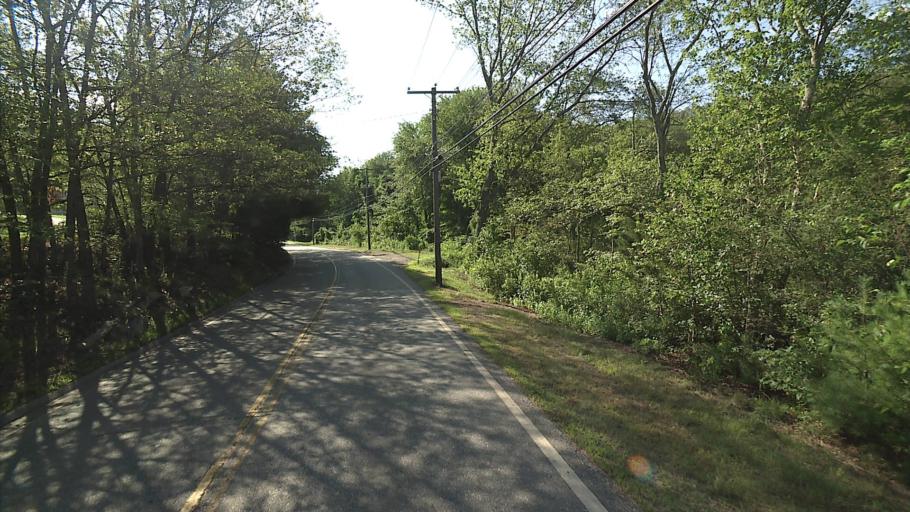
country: US
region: Connecticut
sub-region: New London County
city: Montville Center
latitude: 41.4593
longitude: -72.1470
